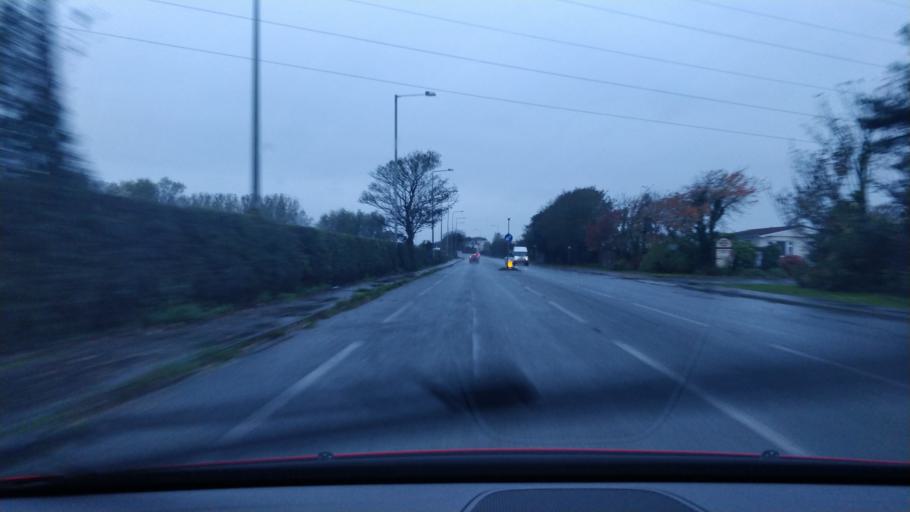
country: GB
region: England
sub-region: Lancashire
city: Poulton le Fylde
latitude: 53.7868
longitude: -2.9715
